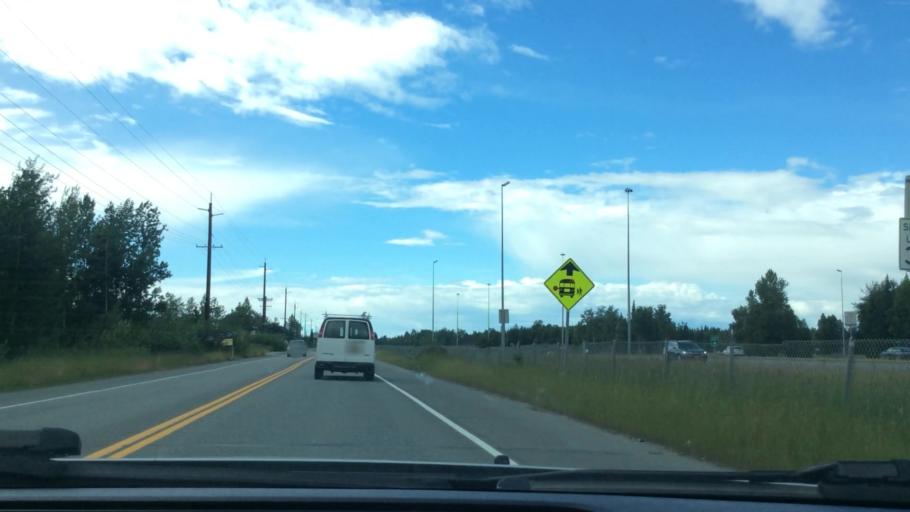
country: US
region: Alaska
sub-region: Anchorage Municipality
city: Anchorage
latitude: 61.2242
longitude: -149.7686
